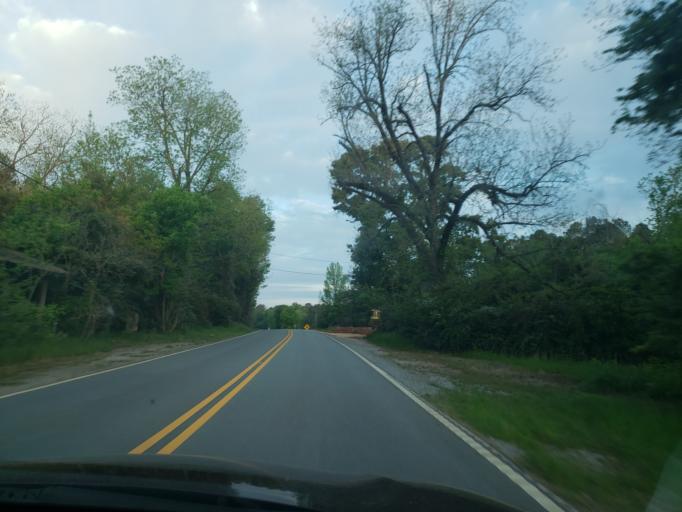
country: US
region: Alabama
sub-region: Tallapoosa County
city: Dadeville
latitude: 32.7014
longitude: -85.7447
